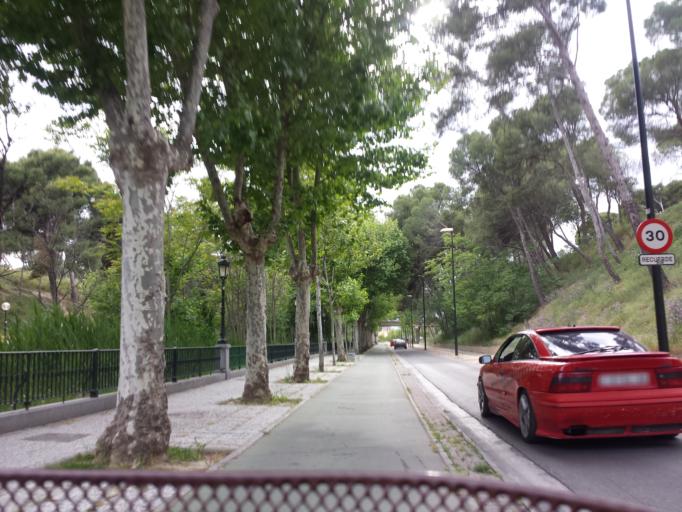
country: ES
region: Aragon
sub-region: Provincia de Zaragoza
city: Delicias
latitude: 41.6299
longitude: -0.8932
